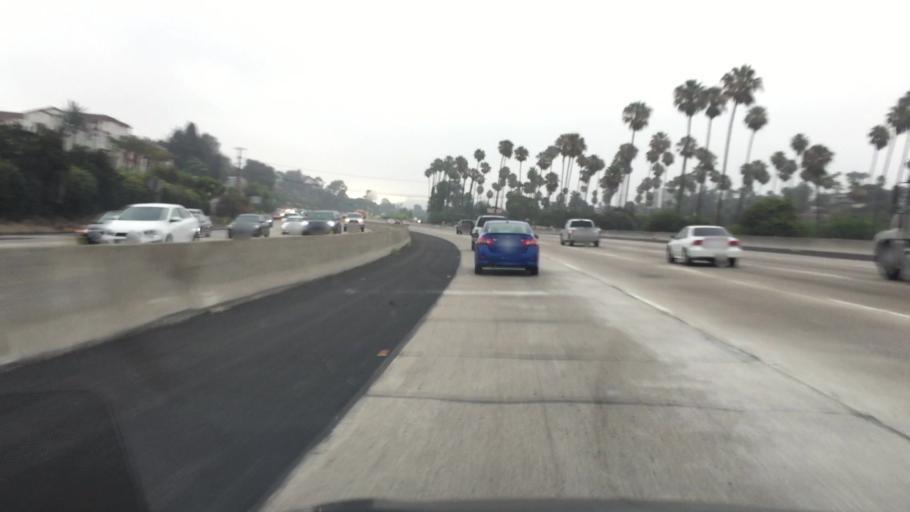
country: US
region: California
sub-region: San Diego County
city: La Mesa
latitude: 32.7726
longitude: -117.0407
